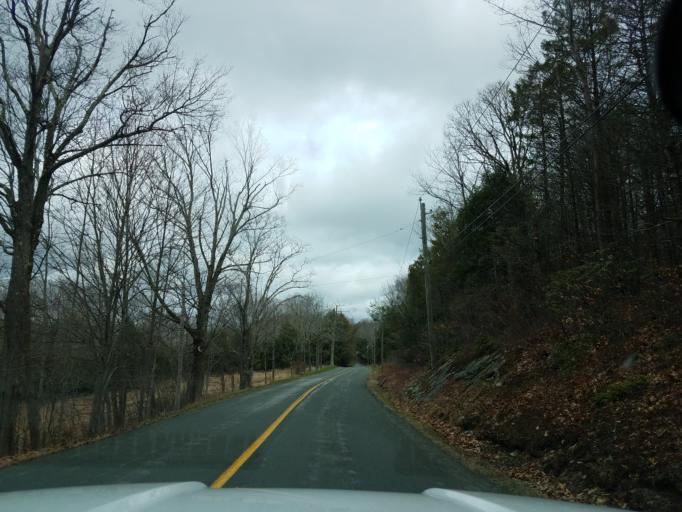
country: US
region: Connecticut
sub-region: Litchfield County
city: Litchfield
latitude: 41.7799
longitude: -73.1769
